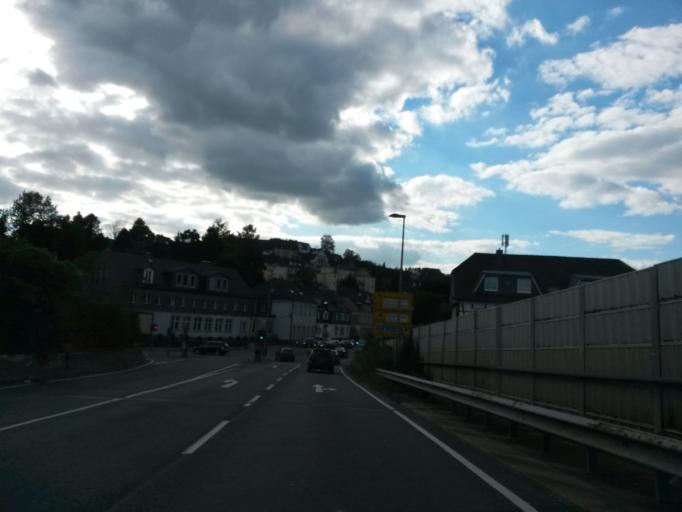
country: DE
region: North Rhine-Westphalia
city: Bergneustadt
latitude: 51.0078
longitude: 7.6253
